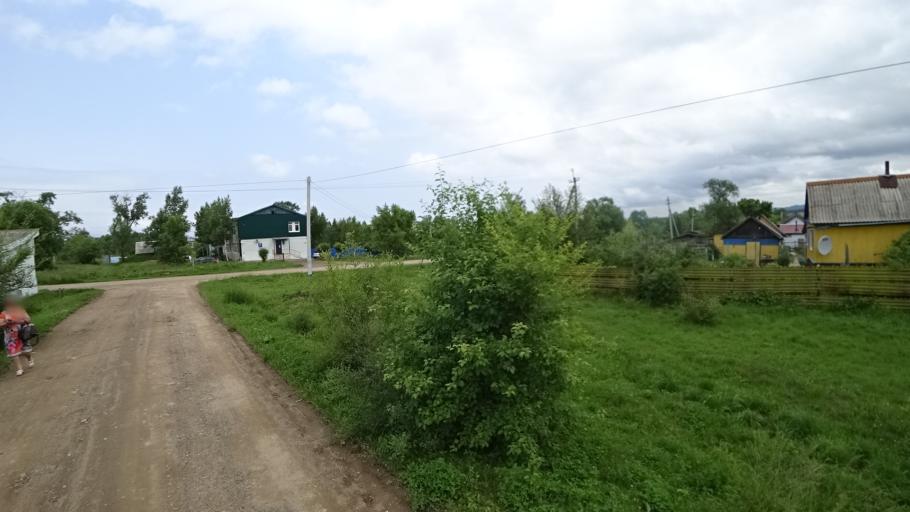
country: RU
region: Primorskiy
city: Novosysoyevka
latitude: 44.2360
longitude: 133.3643
